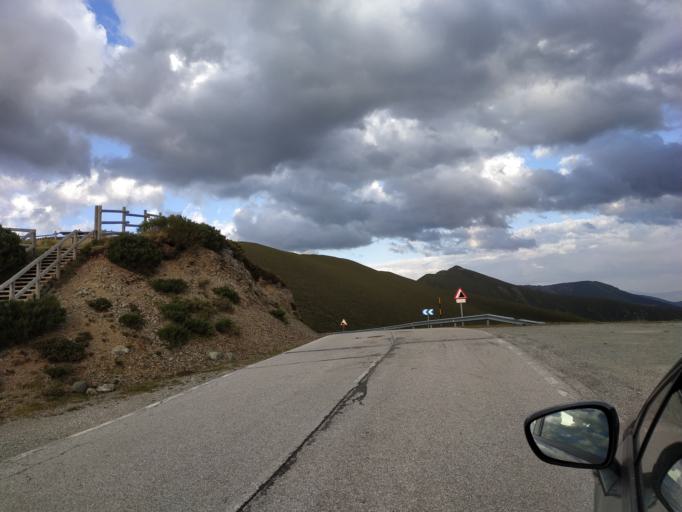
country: ES
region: Castille and Leon
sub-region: Provincia de Leon
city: Candin
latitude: 42.8685
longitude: -6.8182
